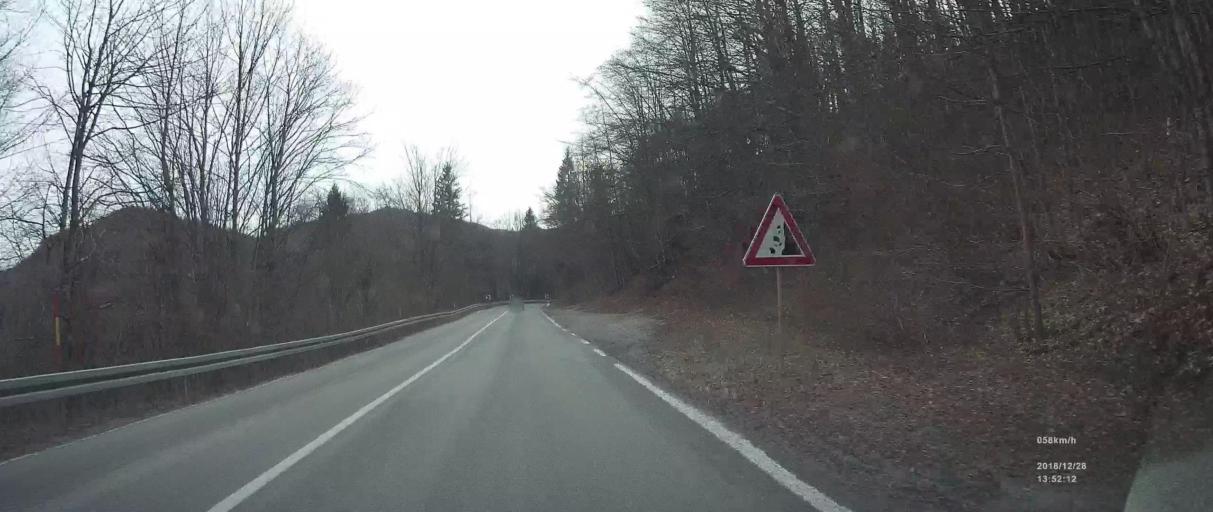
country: HR
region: Primorsko-Goranska
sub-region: Grad Delnice
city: Delnice
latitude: 45.3925
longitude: 14.8463
